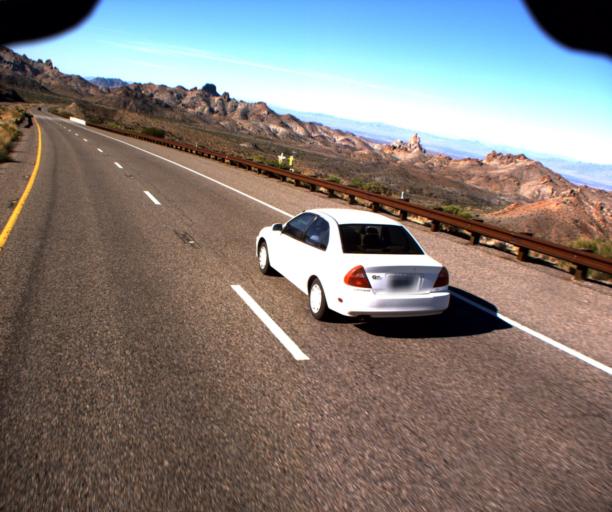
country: US
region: Nevada
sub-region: Clark County
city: Laughlin
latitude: 35.2079
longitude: -114.4032
